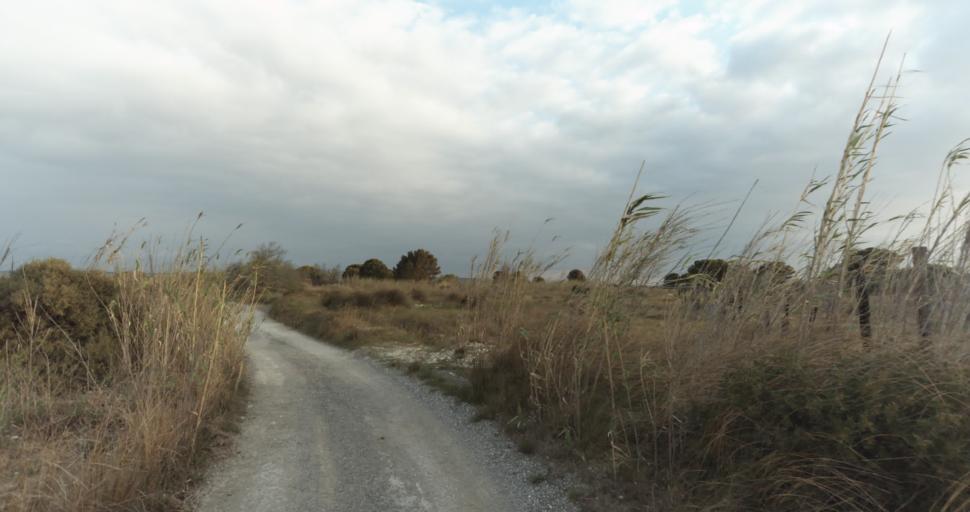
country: FR
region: Languedoc-Roussillon
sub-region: Departement de l'Aude
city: Leucate
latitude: 42.9523
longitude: 3.0327
